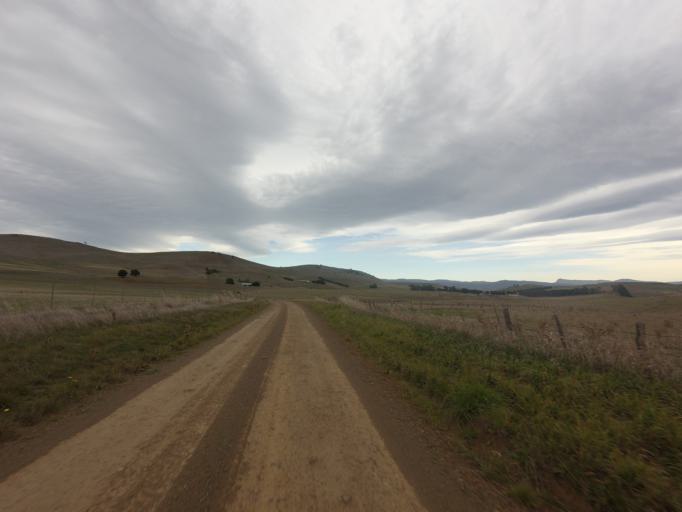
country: AU
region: Tasmania
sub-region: Derwent Valley
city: New Norfolk
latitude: -42.4435
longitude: 146.7992
